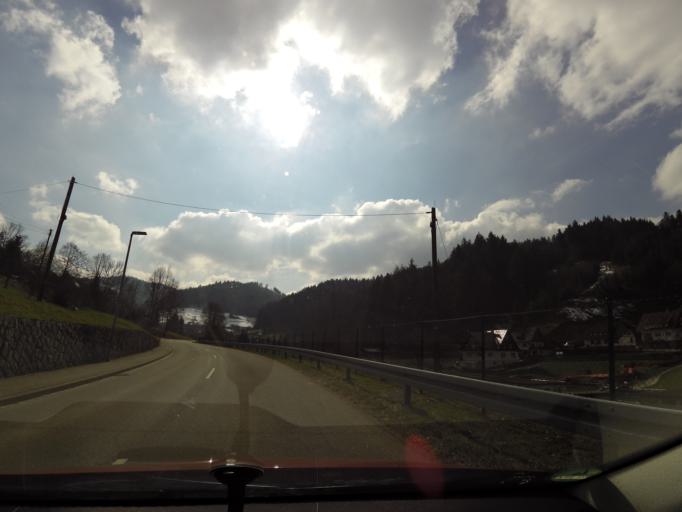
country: DE
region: Baden-Wuerttemberg
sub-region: Freiburg Region
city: Ottenhofen im Schwarzwald
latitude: 48.5607
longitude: 8.1530
